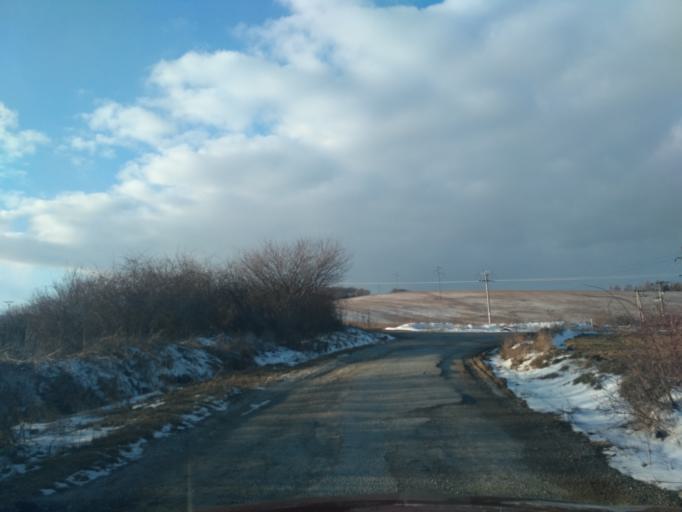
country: SK
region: Kosicky
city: Kosice
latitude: 48.7331
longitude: 21.1466
